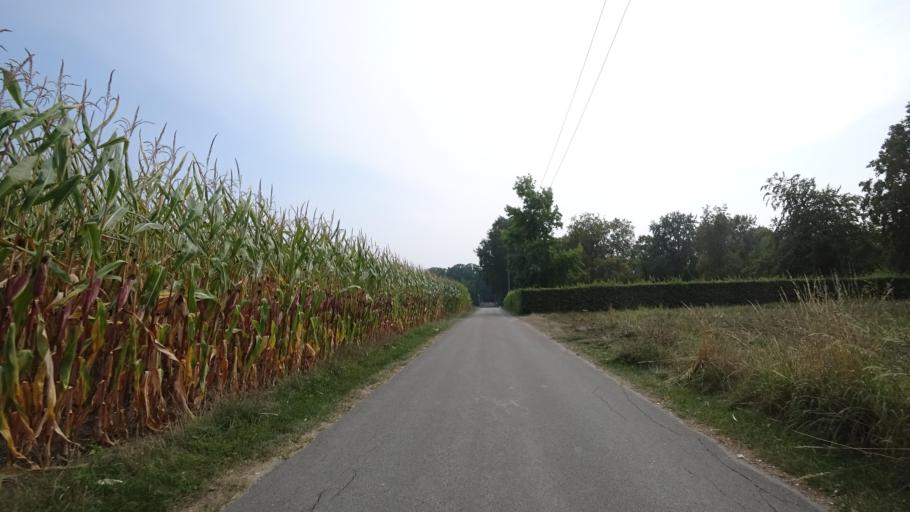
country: DE
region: North Rhine-Westphalia
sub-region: Regierungsbezirk Detmold
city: Guetersloh
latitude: 51.9167
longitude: 8.4387
